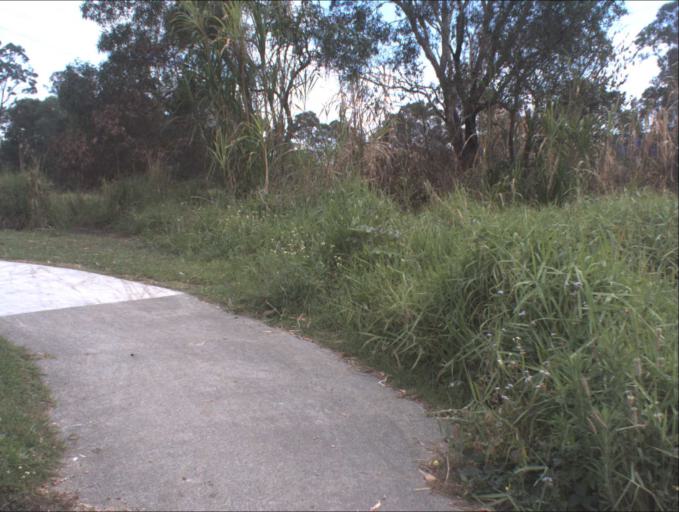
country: AU
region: Queensland
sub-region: Logan
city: Slacks Creek
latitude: -27.6404
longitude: 153.1342
